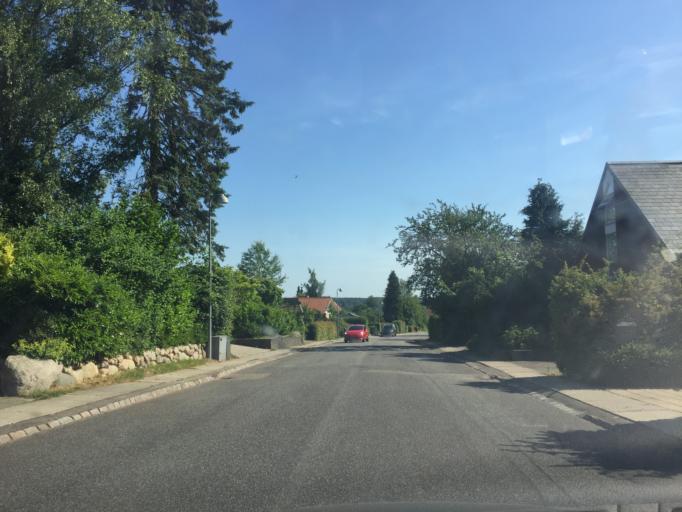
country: DK
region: Capital Region
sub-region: Fureso Kommune
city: Vaerlose
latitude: 55.7808
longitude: 12.3598
